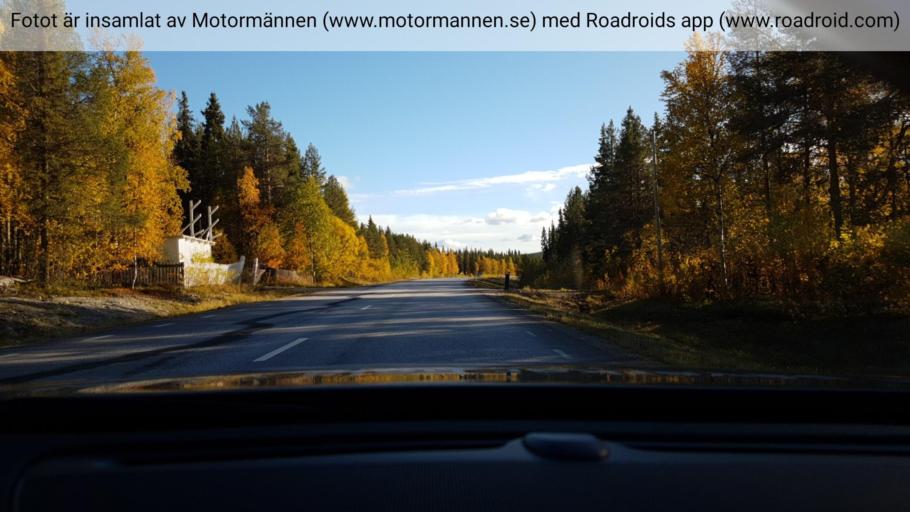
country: SE
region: Norrbotten
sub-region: Jokkmokks Kommun
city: Jokkmokk
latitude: 66.9760
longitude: 19.8377
